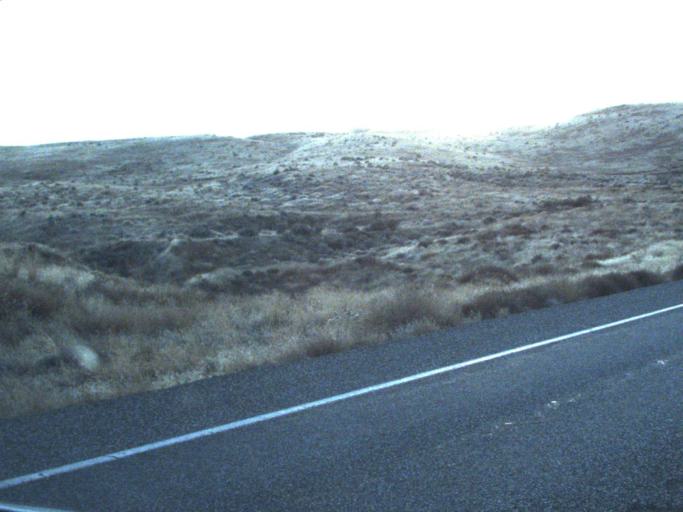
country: US
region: Washington
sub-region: Benton County
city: Finley
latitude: 46.0687
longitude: -118.8085
